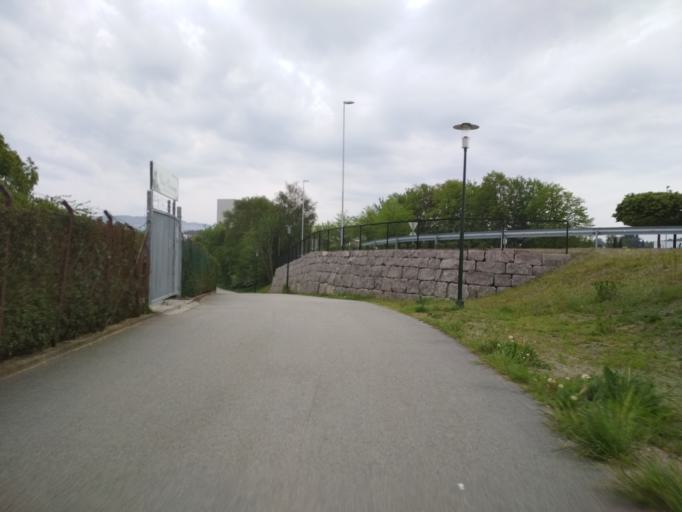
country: NO
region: Rogaland
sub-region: Stavanger
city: Stavanger
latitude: 58.9528
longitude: 5.7227
